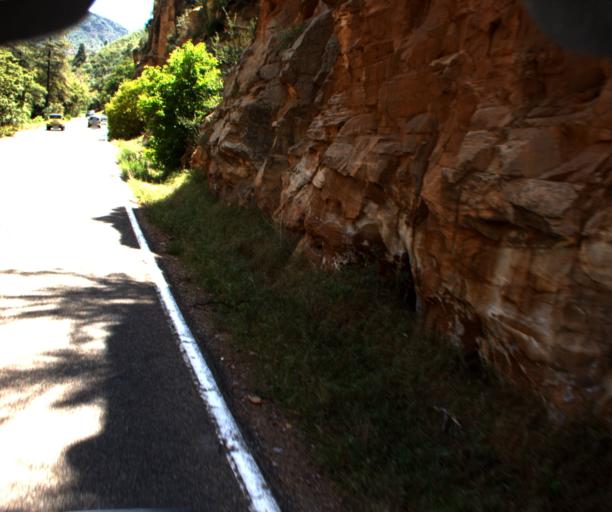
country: US
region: Arizona
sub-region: Coconino County
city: Sedona
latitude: 34.9227
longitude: -111.7352
